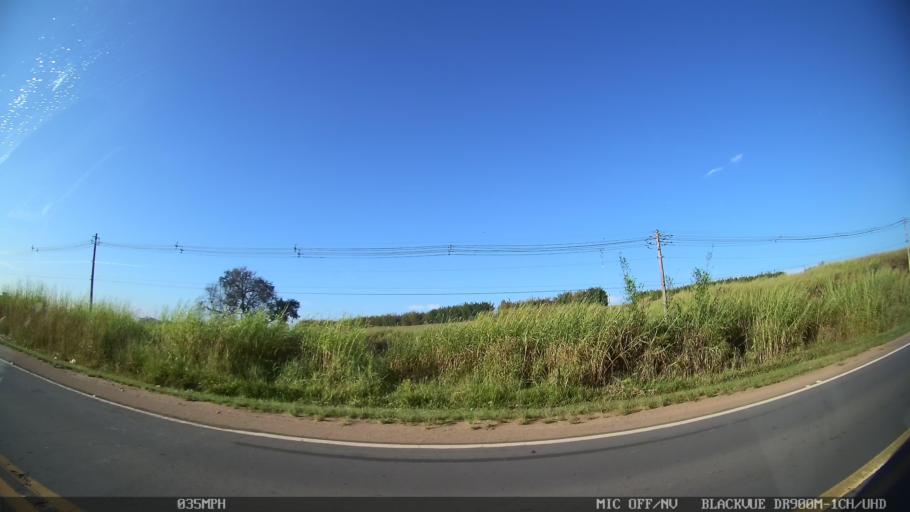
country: BR
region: Sao Paulo
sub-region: Vinhedo
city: Vinhedo
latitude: -23.0542
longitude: -47.0569
